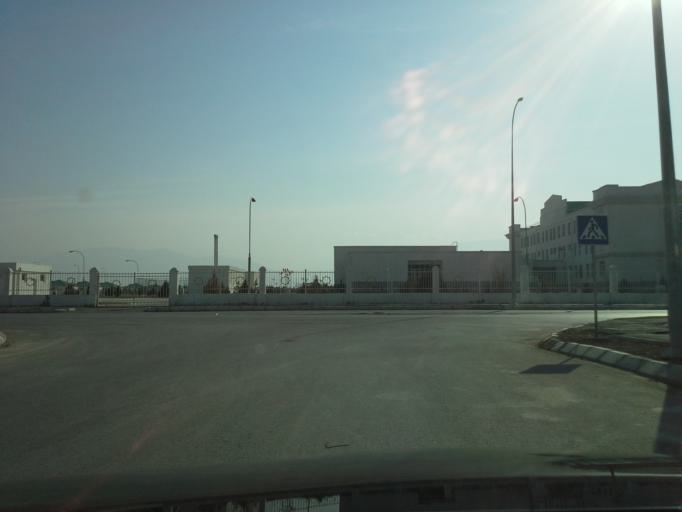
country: TM
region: Ahal
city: Abadan
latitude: 38.1717
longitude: 58.0482
